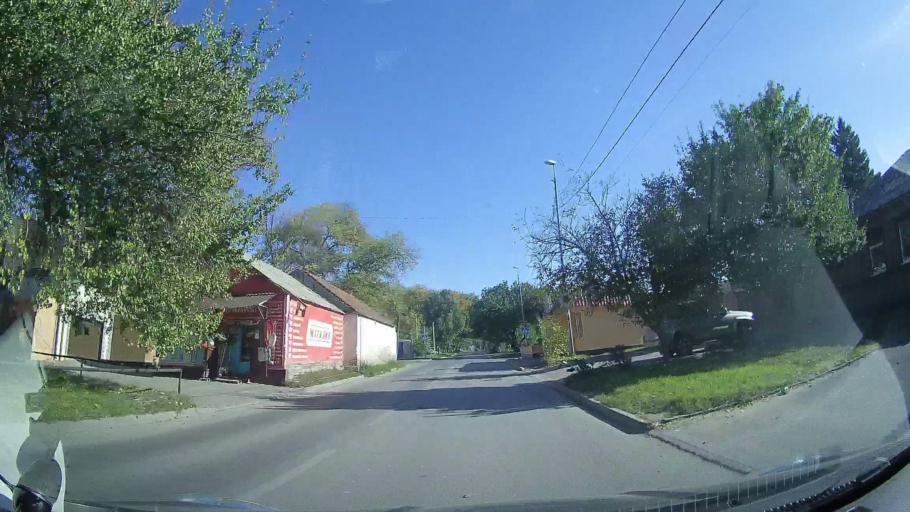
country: RU
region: Rostov
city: Rostov-na-Donu
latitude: 47.2412
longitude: 39.6743
